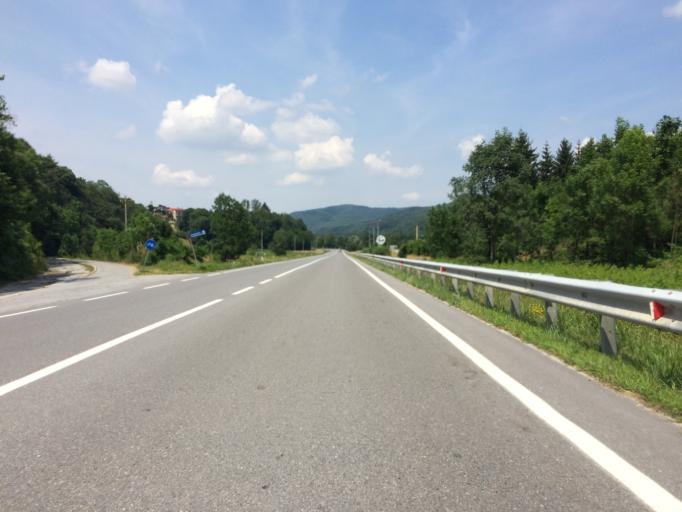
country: IT
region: Piedmont
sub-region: Provincia di Cuneo
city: Robilante
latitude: 44.2692
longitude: 7.5189
